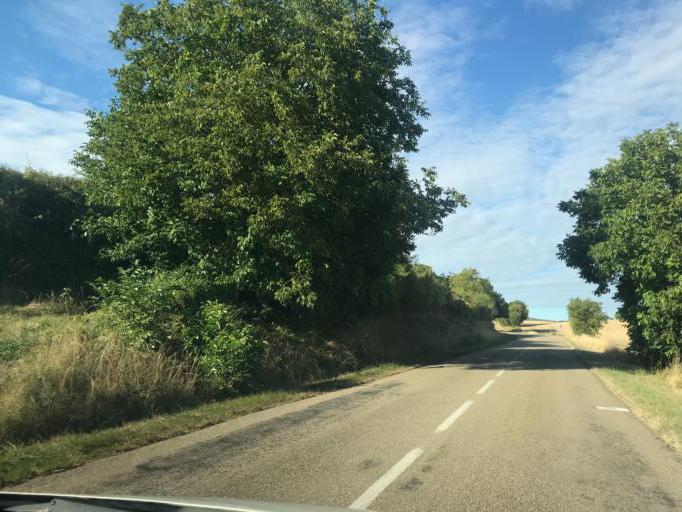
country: FR
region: Bourgogne
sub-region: Departement de l'Yonne
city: Fontenailles
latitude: 47.5539
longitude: 3.4298
